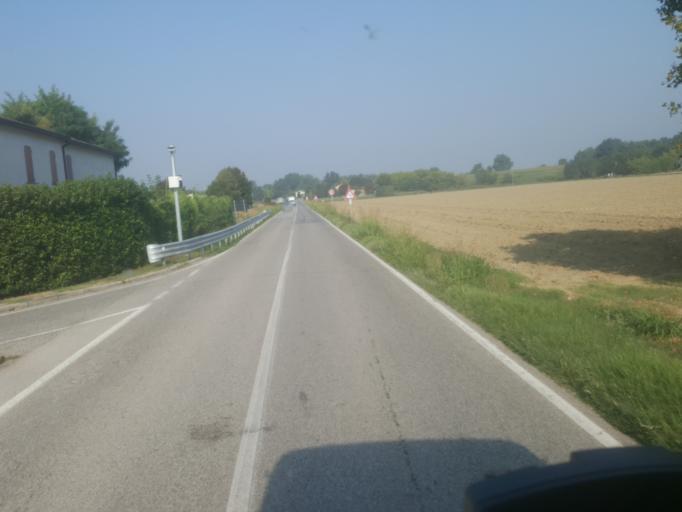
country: IT
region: Emilia-Romagna
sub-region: Provincia di Ravenna
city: Voltana
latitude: 44.5528
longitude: 11.9441
